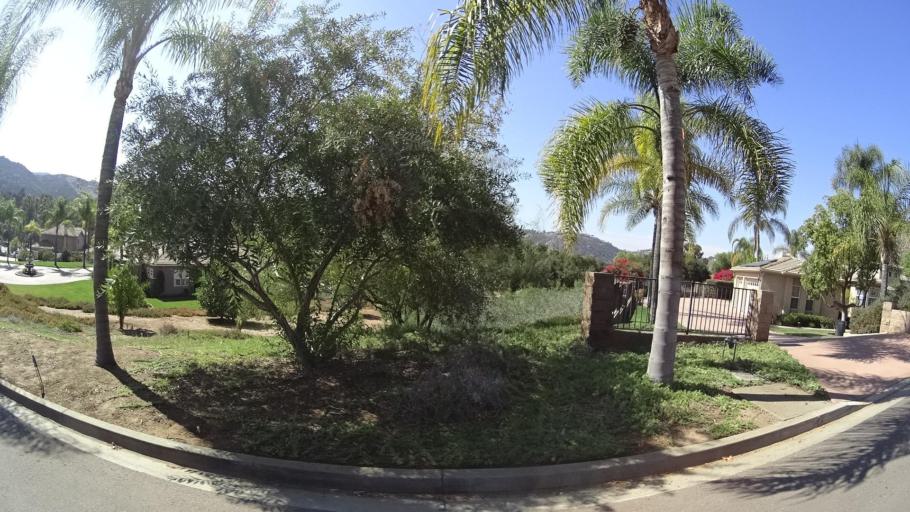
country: US
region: California
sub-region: San Diego County
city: Crest
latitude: 32.7827
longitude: -116.8738
